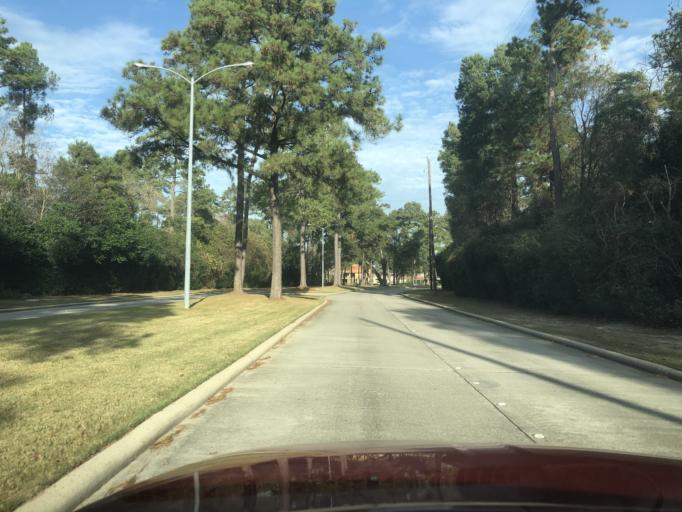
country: US
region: Texas
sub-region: Harris County
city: Spring
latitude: 30.0017
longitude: -95.4757
